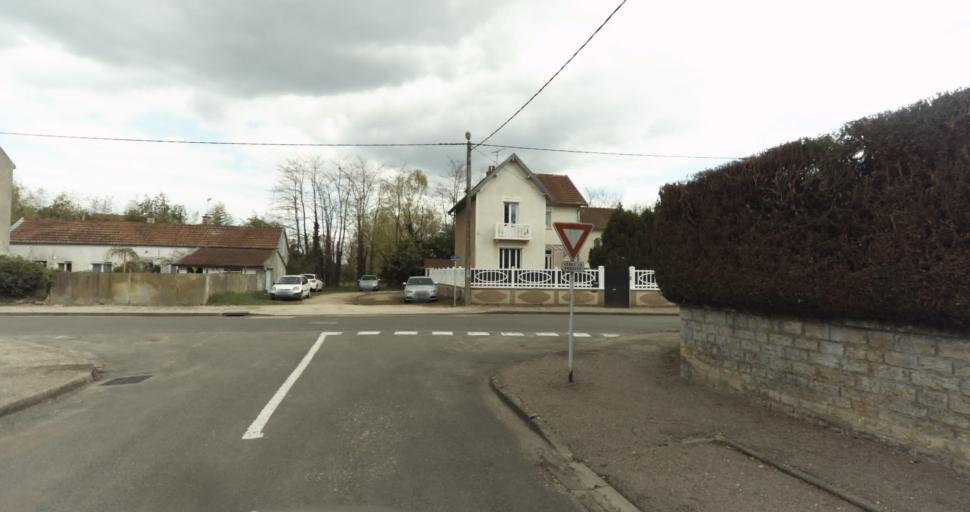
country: FR
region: Bourgogne
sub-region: Departement de la Cote-d'Or
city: Auxonne
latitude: 47.1929
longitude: 5.3924
